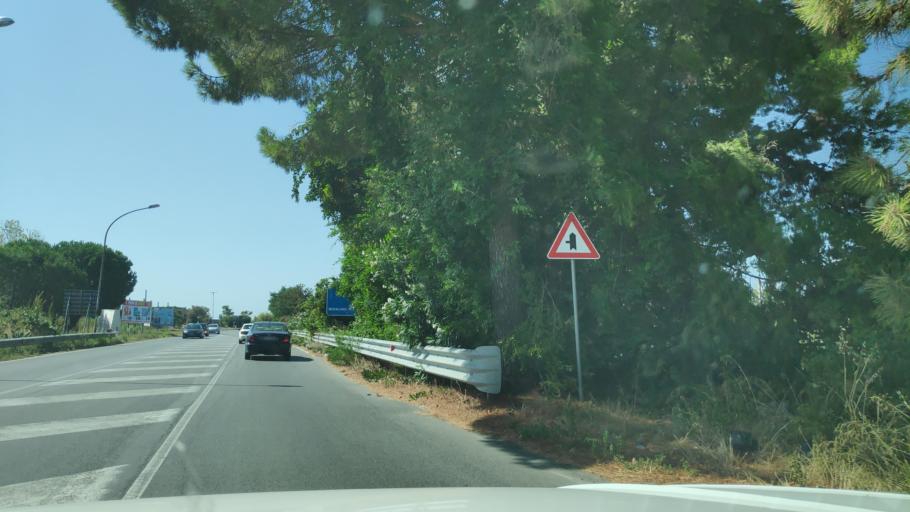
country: IT
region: Calabria
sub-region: Provincia di Reggio Calabria
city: Bovalino
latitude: 38.1399
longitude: 16.1655
